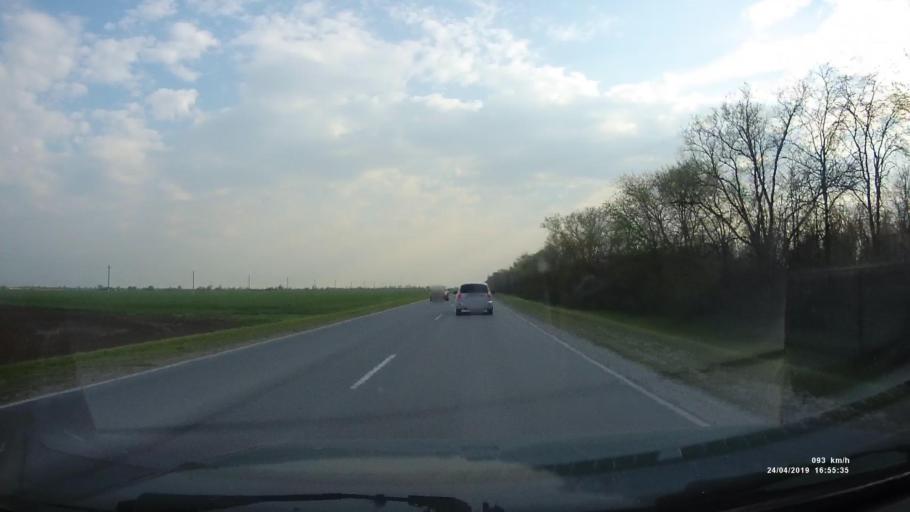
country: RU
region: Rostov
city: Proletarsk
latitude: 46.6623
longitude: 41.6866
